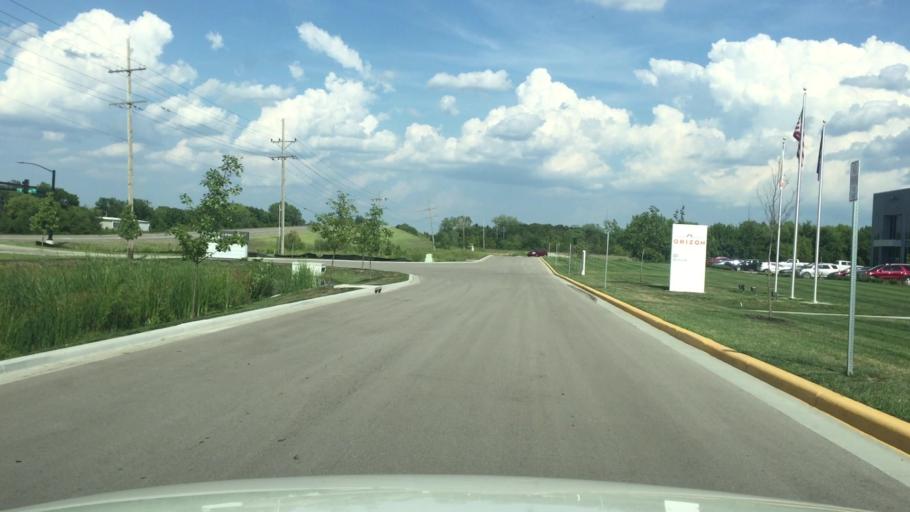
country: US
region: Kansas
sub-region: Johnson County
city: Olathe
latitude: 38.8671
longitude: -94.8301
